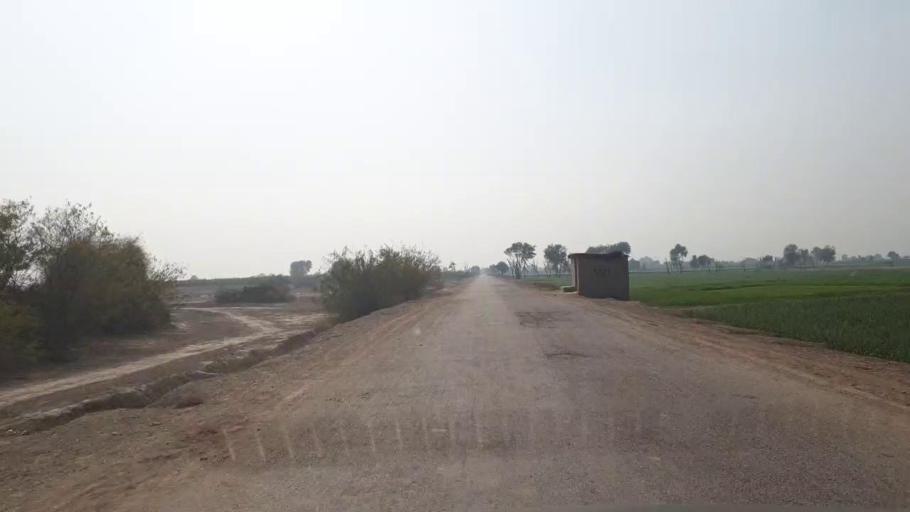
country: PK
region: Sindh
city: Hala
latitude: 25.8712
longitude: 68.4316
